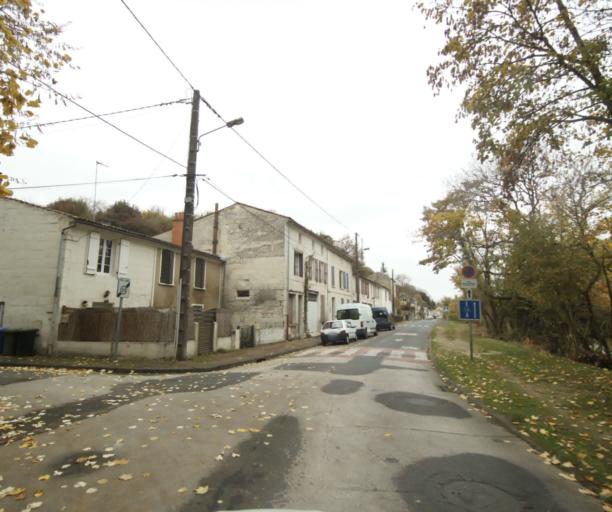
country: FR
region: Poitou-Charentes
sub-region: Departement de la Charente-Maritime
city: Saintes
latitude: 45.7348
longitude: -0.6399
